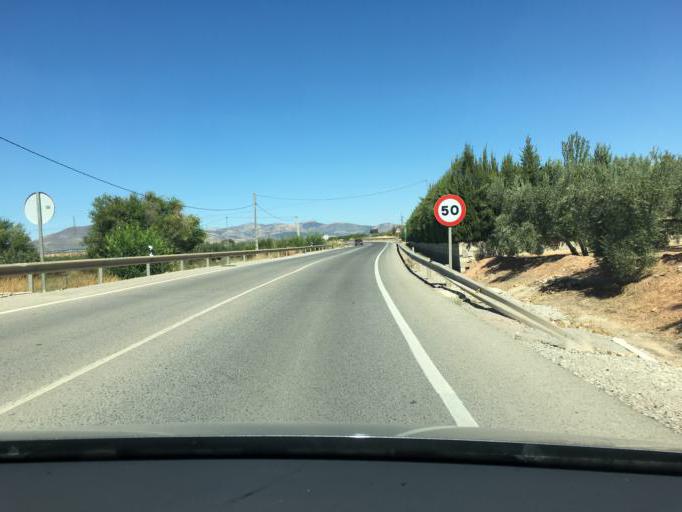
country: ES
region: Andalusia
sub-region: Provincia de Granada
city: Albolote
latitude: 37.2605
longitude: -3.6607
